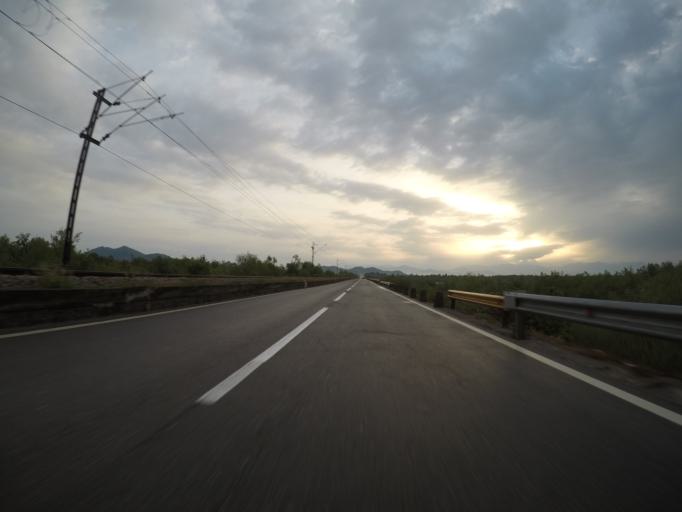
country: ME
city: Mojanovici
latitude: 42.2832
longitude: 19.1408
